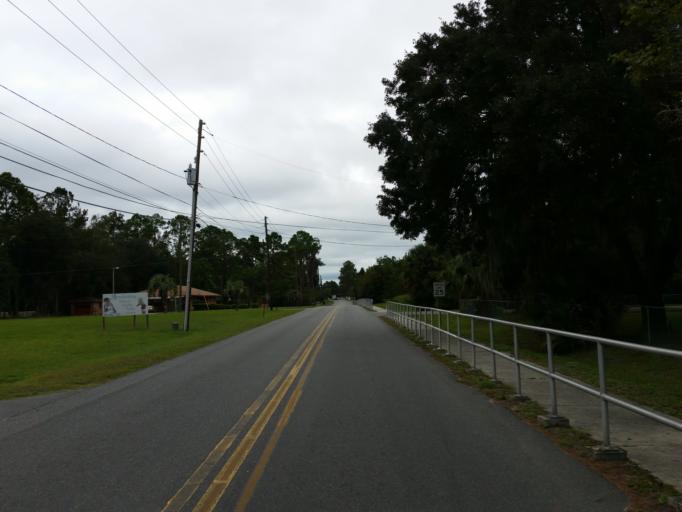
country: US
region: Florida
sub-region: Hamilton County
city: Jasper
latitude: 30.5180
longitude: -82.9598
